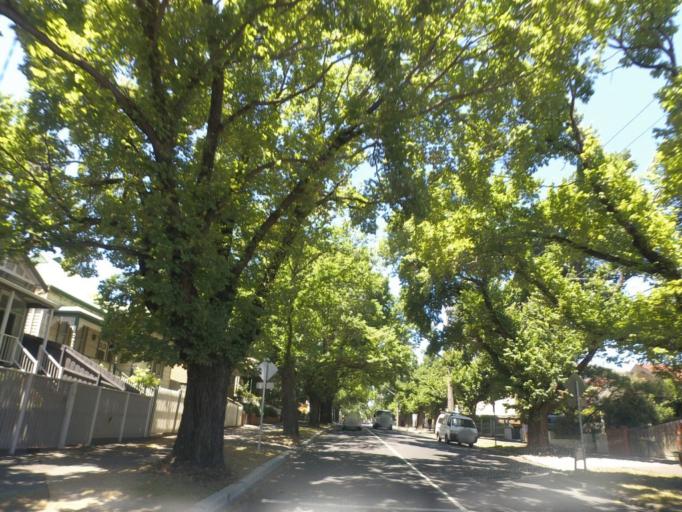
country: AU
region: Victoria
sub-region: Moonee Valley
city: Flemington
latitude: -37.7913
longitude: 144.9251
